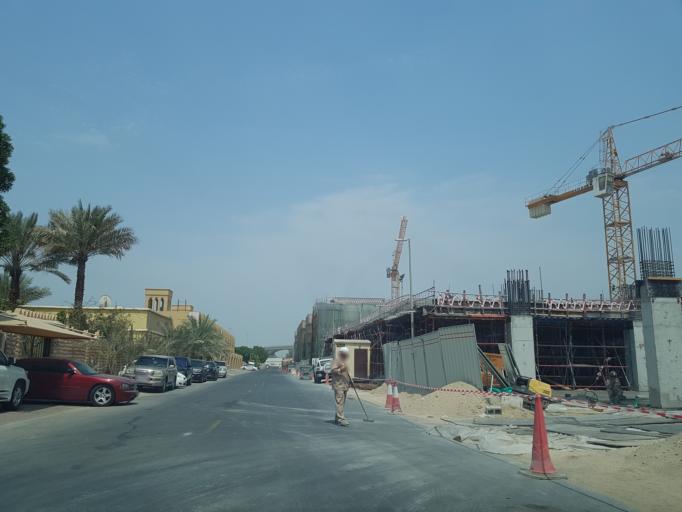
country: AE
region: Ash Shariqah
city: Sharjah
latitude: 25.2337
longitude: 55.3817
